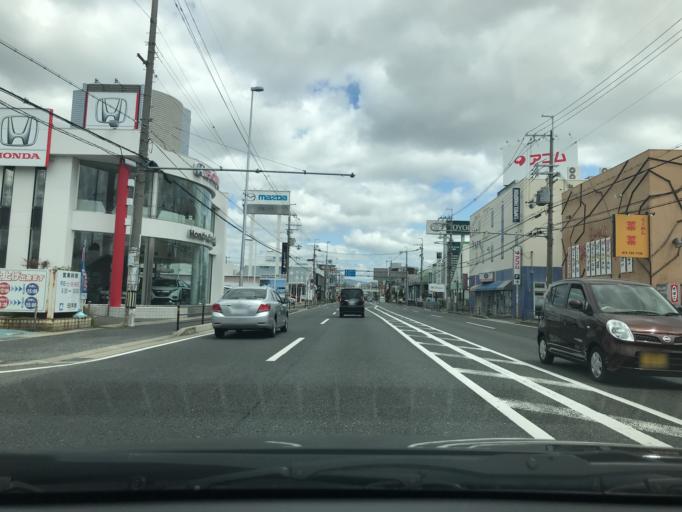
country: JP
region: Osaka
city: Mino
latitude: 34.8229
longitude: 135.4739
